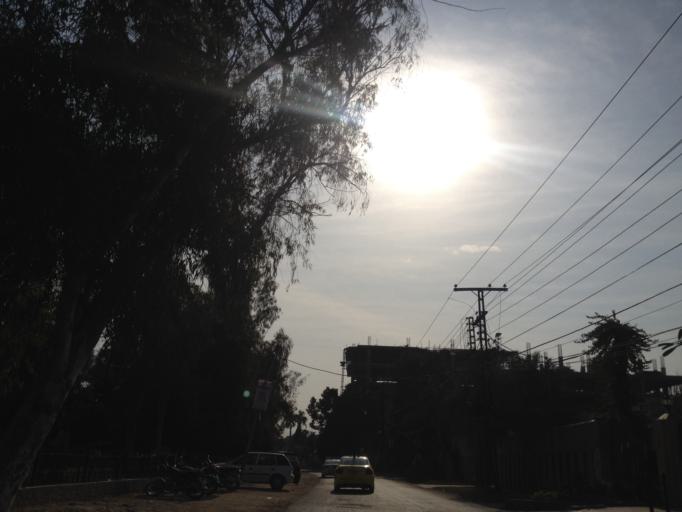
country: PK
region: Punjab
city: Lahore
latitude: 31.5071
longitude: 74.3194
